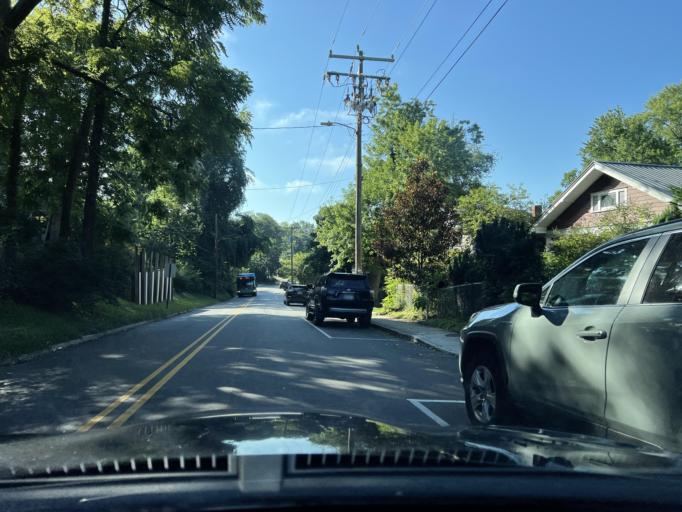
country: US
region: North Carolina
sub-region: Buncombe County
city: Asheville
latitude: 35.5765
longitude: -82.5864
